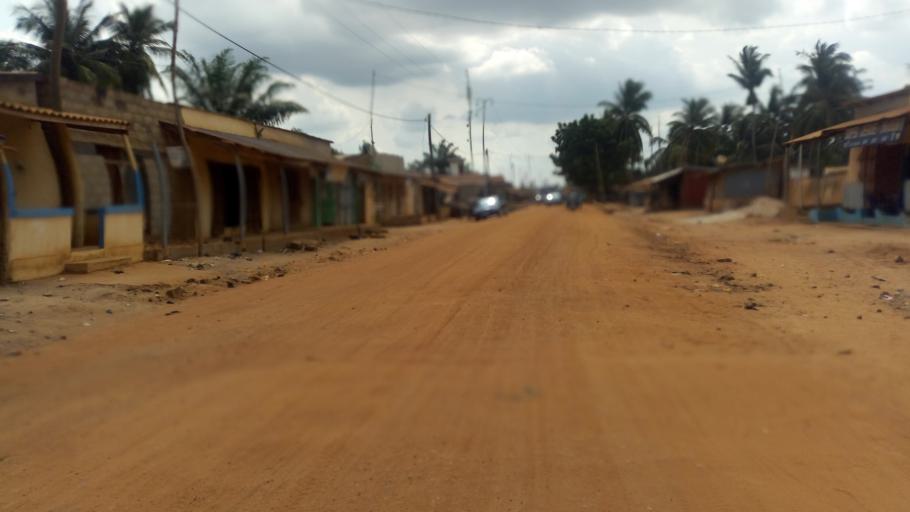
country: TG
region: Maritime
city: Tsevie
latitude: 6.3215
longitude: 1.2215
